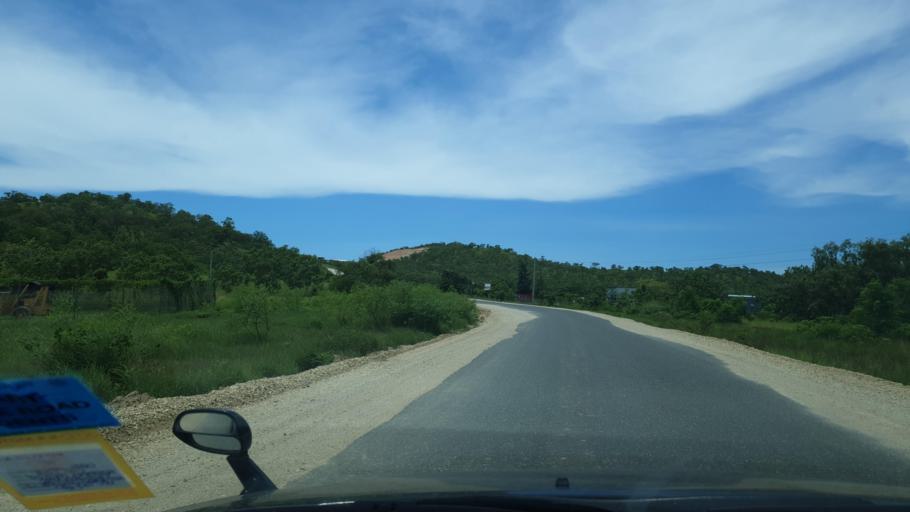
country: PG
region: National Capital
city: Port Moresby
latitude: -9.4298
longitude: 147.0745
